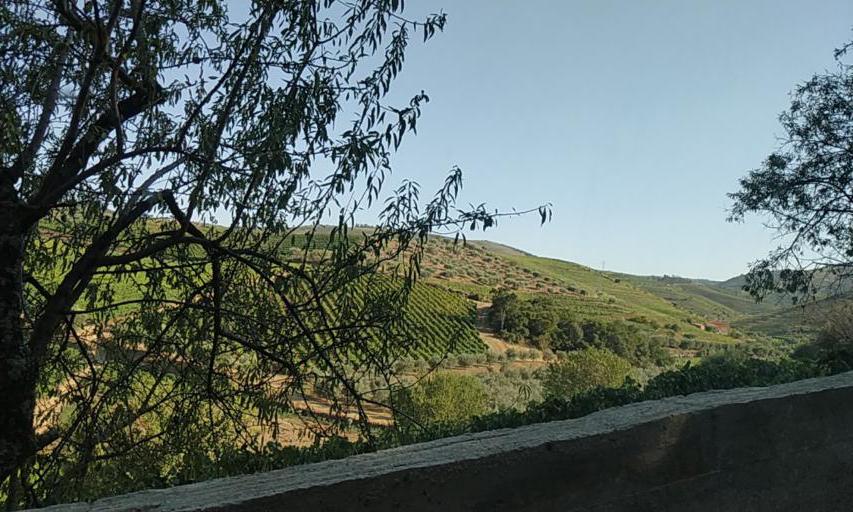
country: PT
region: Viseu
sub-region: Sao Joao da Pesqueira
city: Sao Joao da Pesqueira
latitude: 41.1864
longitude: -7.4111
